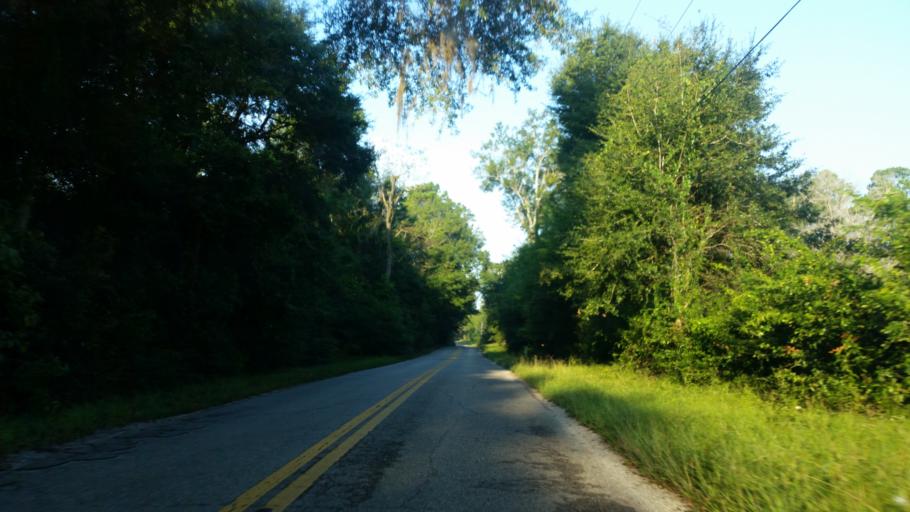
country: US
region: Florida
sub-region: Santa Rosa County
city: East Milton
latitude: 30.6304
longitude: -87.0195
